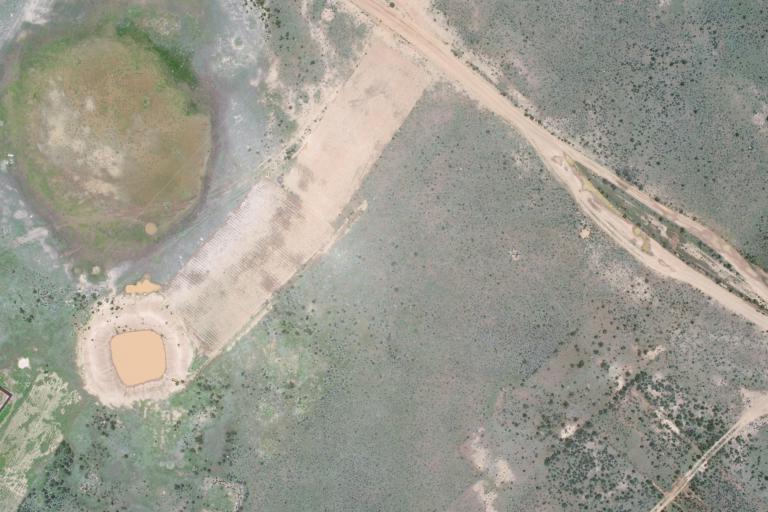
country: BO
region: La Paz
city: Curahuara de Carangas
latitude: -17.2874
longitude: -68.5157
